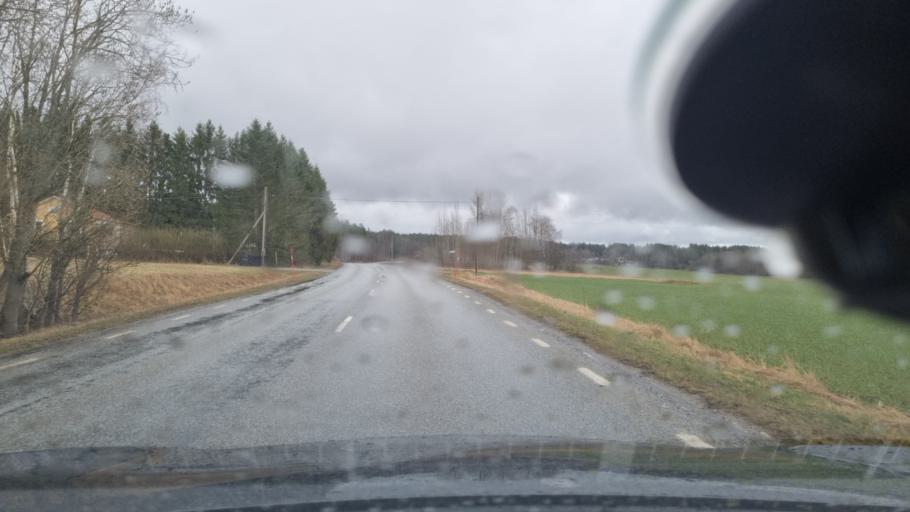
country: SE
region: Stockholm
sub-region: Sigtuna Kommun
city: Sigtuna
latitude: 59.5855
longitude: 17.6628
